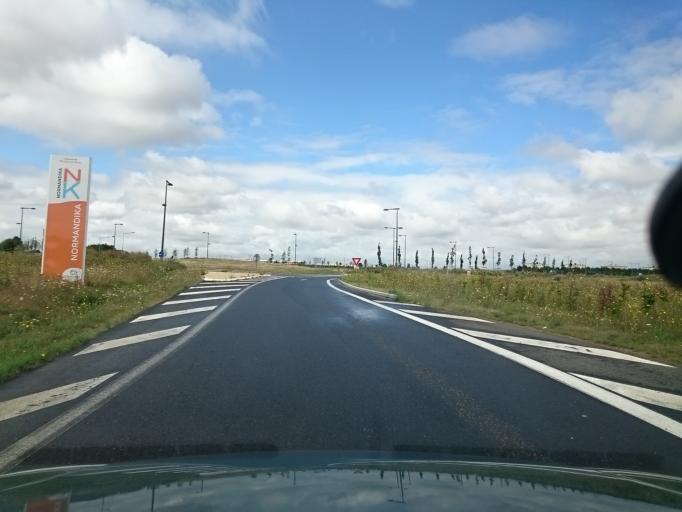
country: FR
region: Lower Normandy
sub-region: Departement du Calvados
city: Fleury-sur-Orne
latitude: 49.1421
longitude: -0.3665
